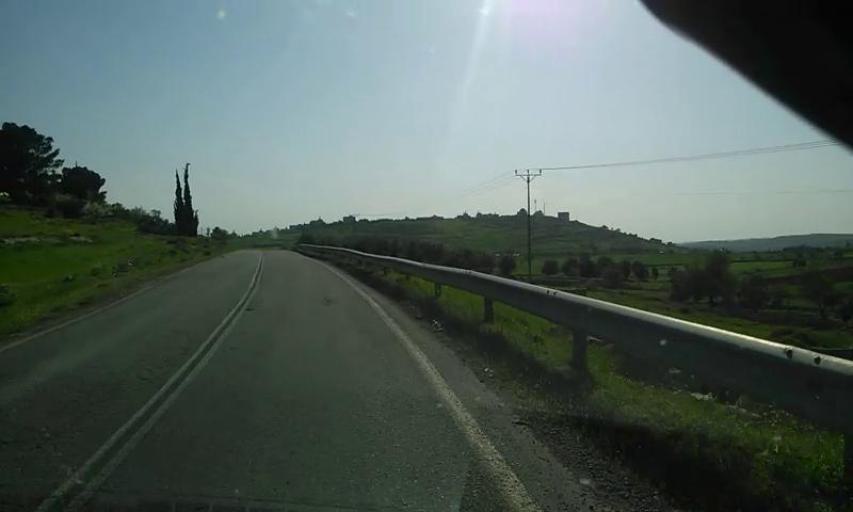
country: PS
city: Al Hilah
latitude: 31.4759
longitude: 35.1323
